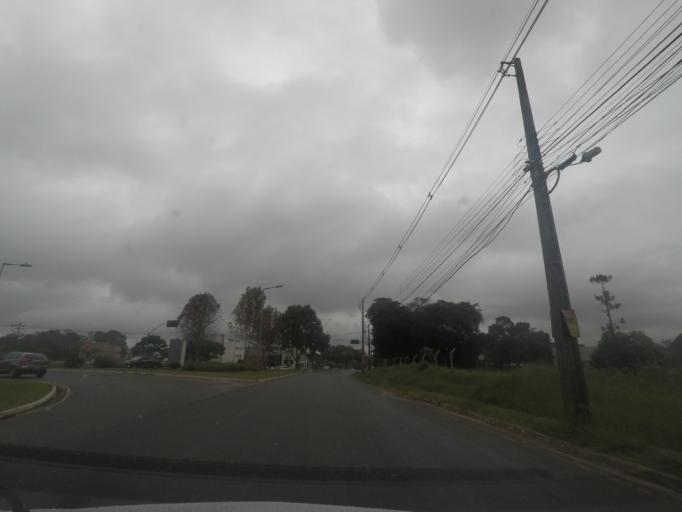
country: BR
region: Parana
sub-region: Pinhais
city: Pinhais
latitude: -25.3920
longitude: -49.1641
